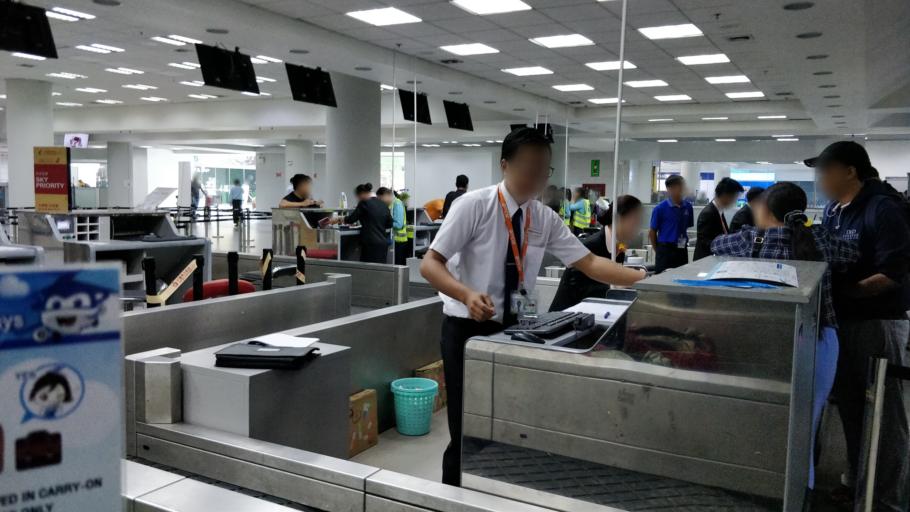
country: MM
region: Sagain
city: Sagaing
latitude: 21.7056
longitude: 95.9703
